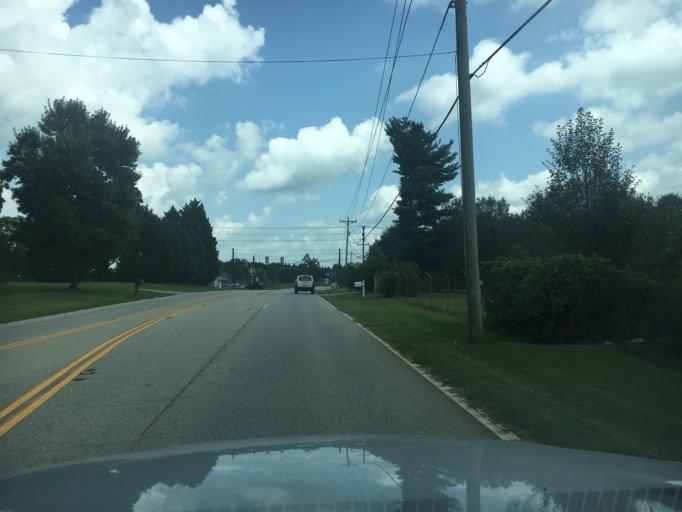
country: US
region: South Carolina
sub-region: Greenville County
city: Five Forks
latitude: 34.8167
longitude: -82.2059
